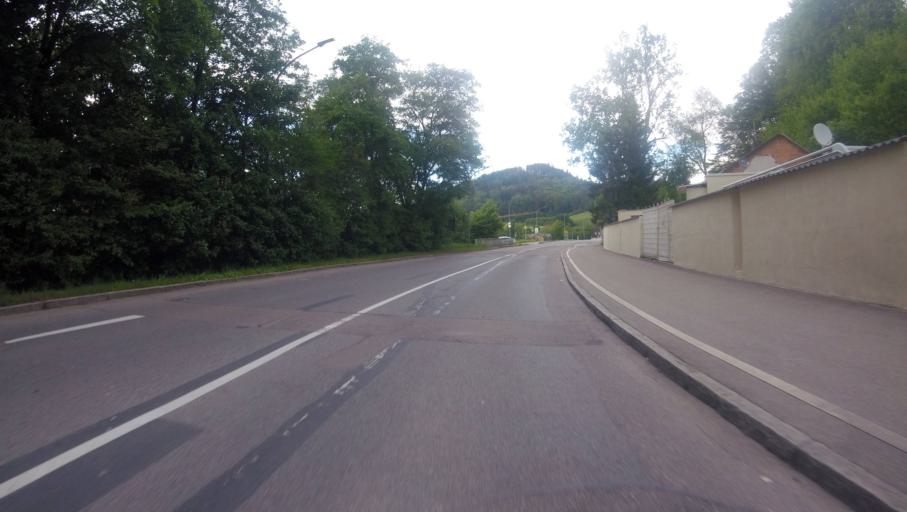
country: DE
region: Baden-Wuerttemberg
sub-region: Regierungsbezirk Stuttgart
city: Murrhardt
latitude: 48.9876
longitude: 9.5525
